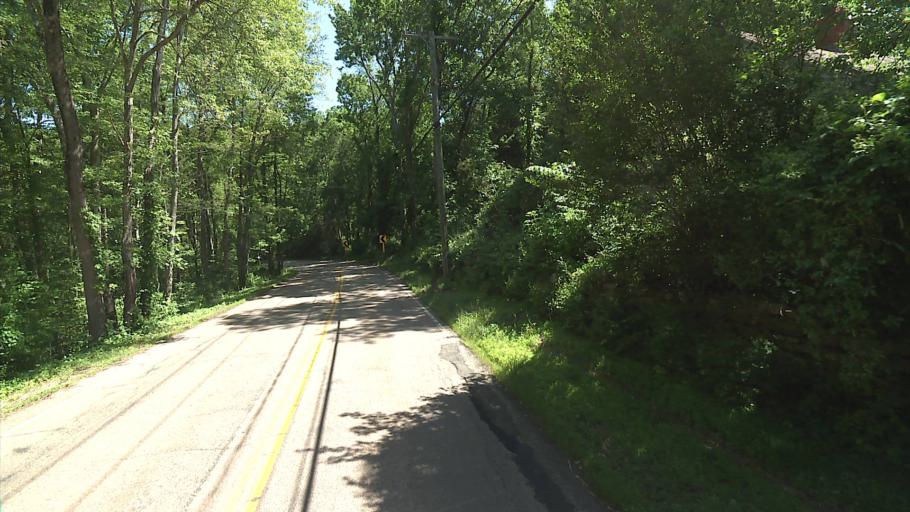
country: US
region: Connecticut
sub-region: New London County
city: Pawcatuck
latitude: 41.4340
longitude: -71.8468
